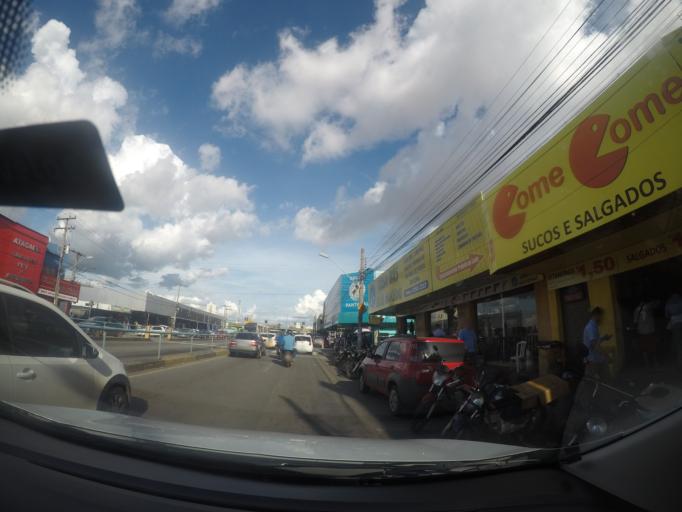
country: BR
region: Goias
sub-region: Goiania
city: Goiania
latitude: -16.6734
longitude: -49.2862
